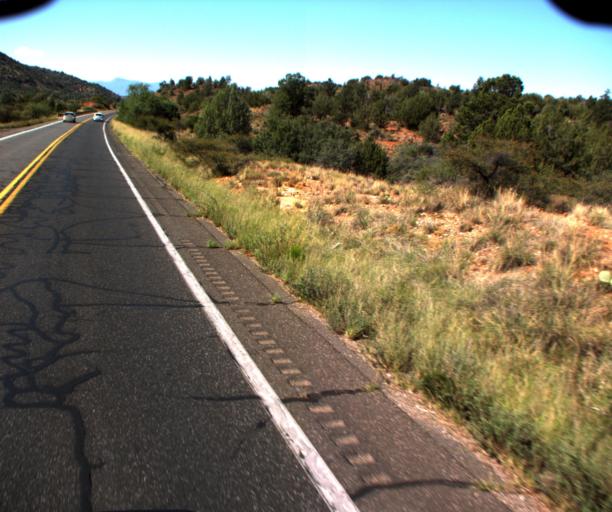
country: US
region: Arizona
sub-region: Yavapai County
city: Big Park
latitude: 34.7494
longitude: -111.7661
